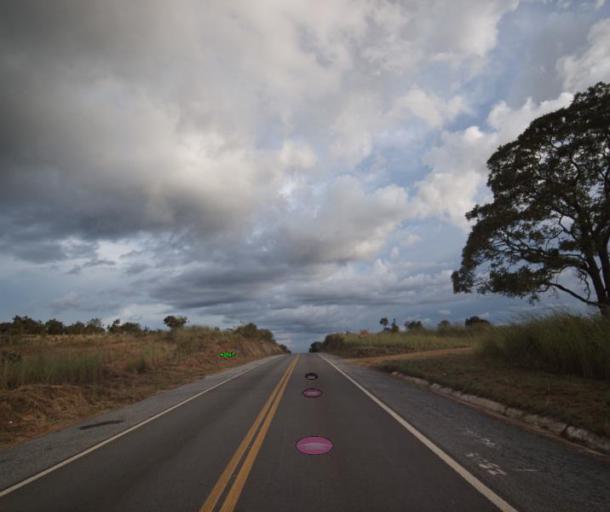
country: BR
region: Goias
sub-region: Barro Alto
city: Barro Alto
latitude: -14.8699
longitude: -48.6399
